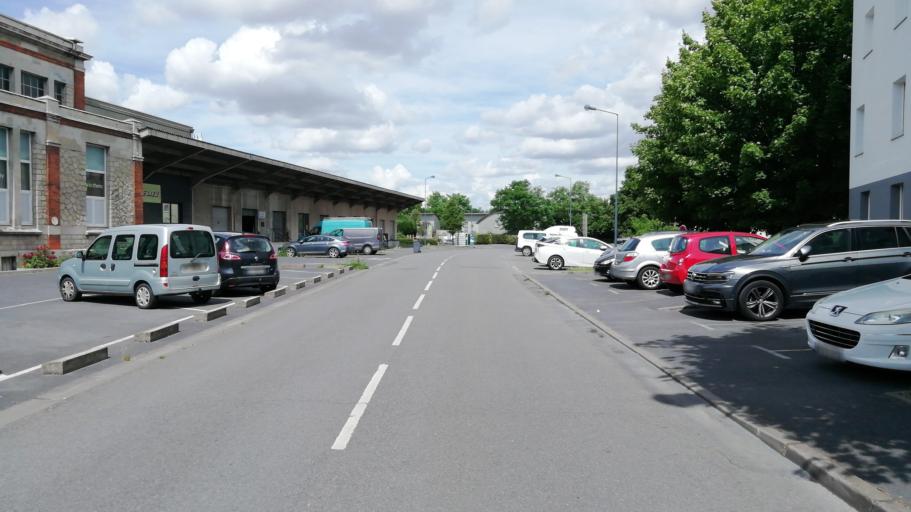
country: FR
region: Champagne-Ardenne
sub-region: Departement de la Marne
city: Betheny
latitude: 49.2717
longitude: 4.0457
